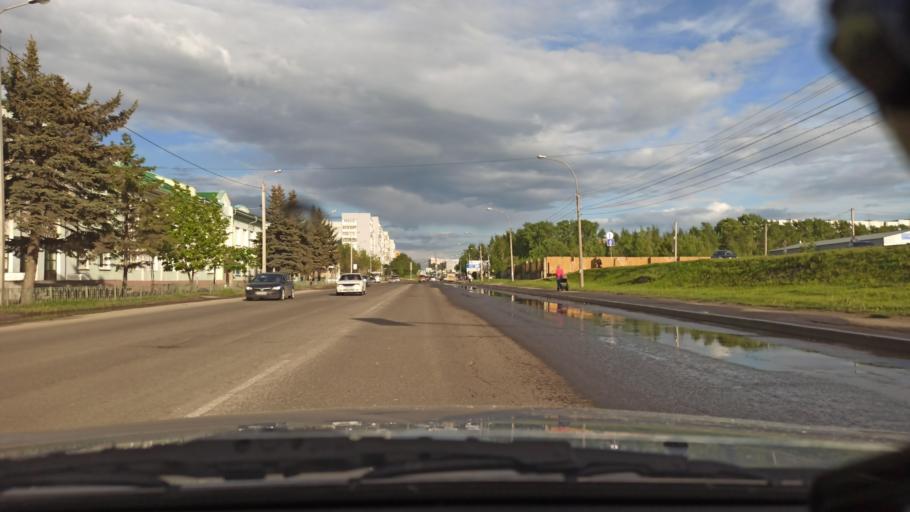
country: RU
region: Vologda
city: Vologda
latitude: 59.2005
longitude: 39.8601
